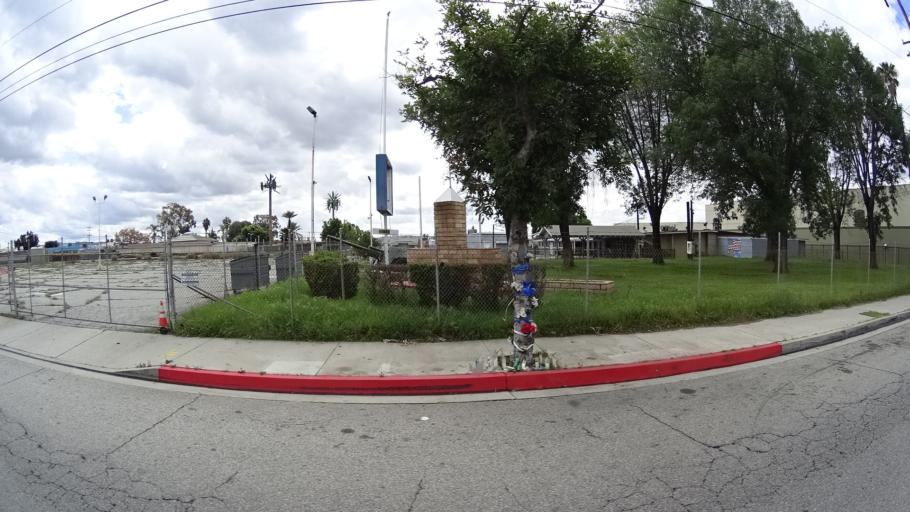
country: US
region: California
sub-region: Los Angeles County
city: Baldwin Park
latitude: 34.0924
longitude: -117.9523
